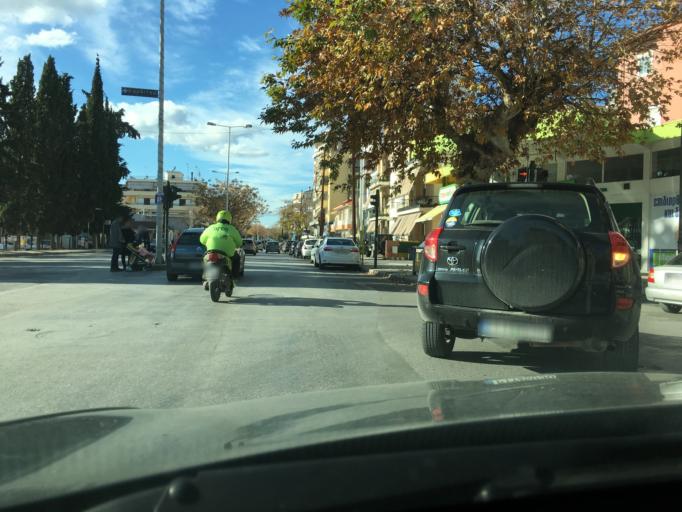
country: GR
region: Thessaly
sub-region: Nomos Larisis
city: Larisa
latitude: 39.6315
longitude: 22.4153
